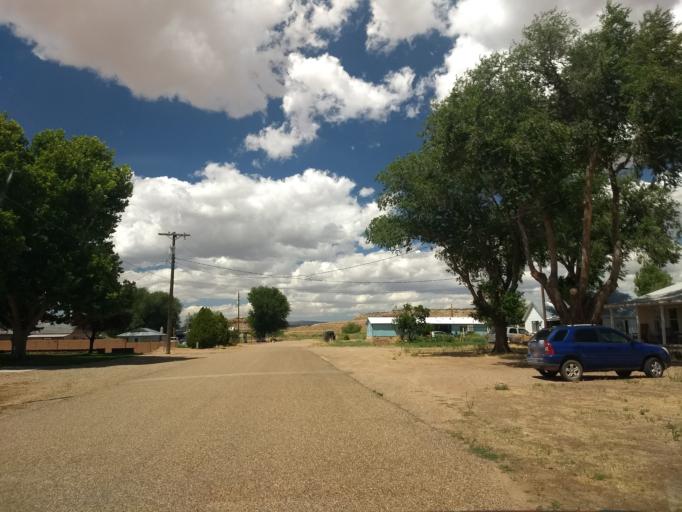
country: US
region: Arizona
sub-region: Coconino County
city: Fredonia
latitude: 36.9474
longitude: -112.5310
